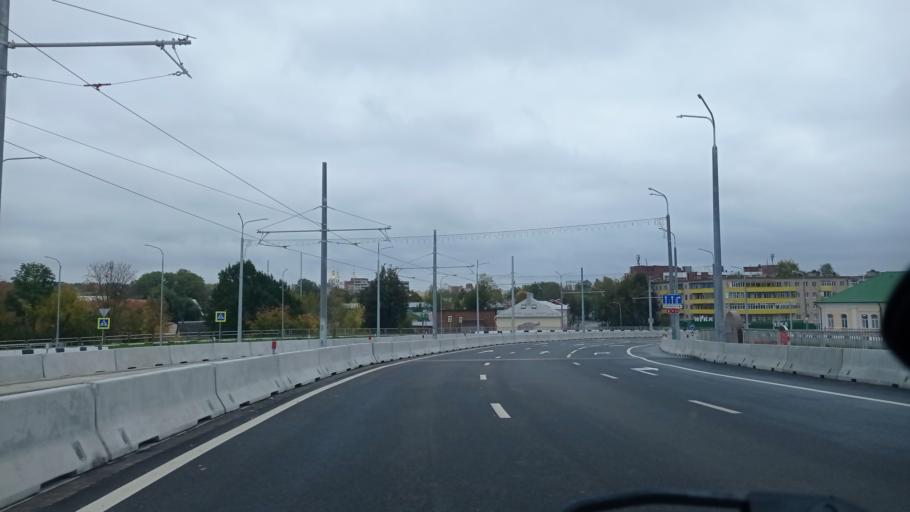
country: BY
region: Vitebsk
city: Vitebsk
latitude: 55.1985
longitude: 30.1874
